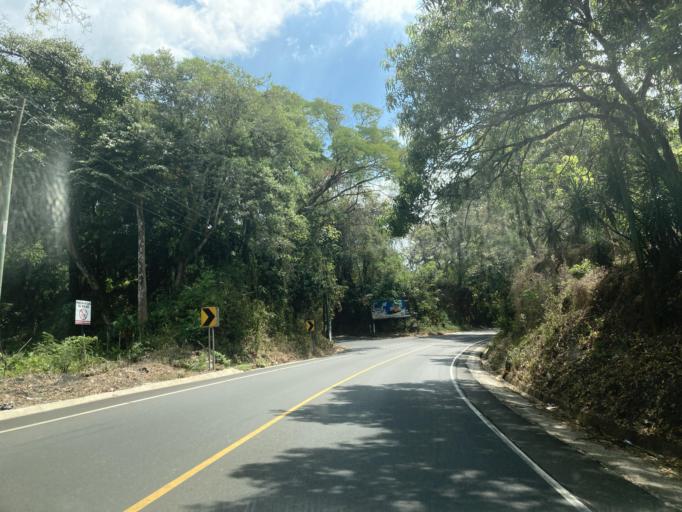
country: GT
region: Santa Rosa
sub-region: Municipio de Taxisco
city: Taxisco
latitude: 14.0754
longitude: -90.4773
